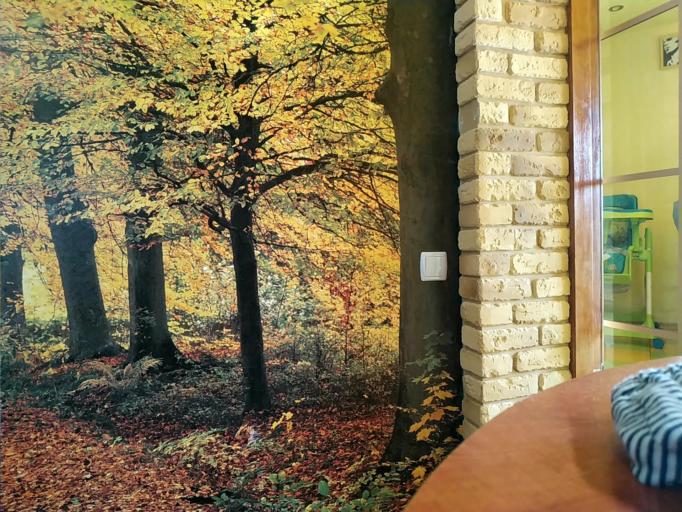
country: RU
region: Novgorod
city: Parfino
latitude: 57.7964
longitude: 31.6284
